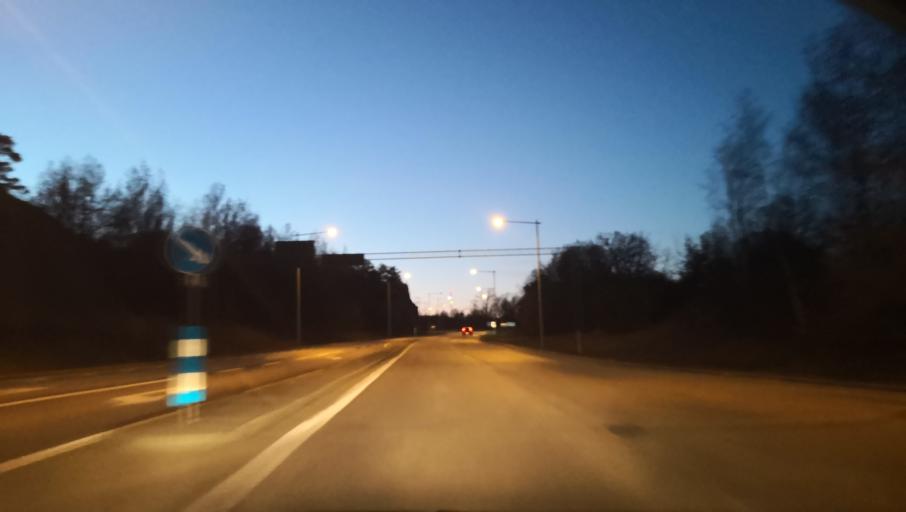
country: SE
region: Stockholm
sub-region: Nynashamns Kommun
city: Nynashamn
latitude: 58.9147
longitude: 17.9566
